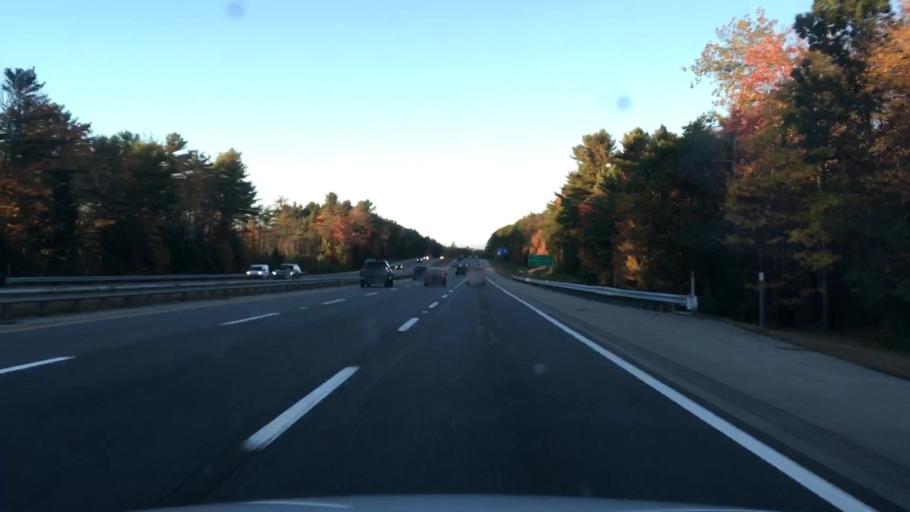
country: US
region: Maine
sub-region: York County
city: Wells Beach Station
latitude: 43.3030
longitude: -70.6152
